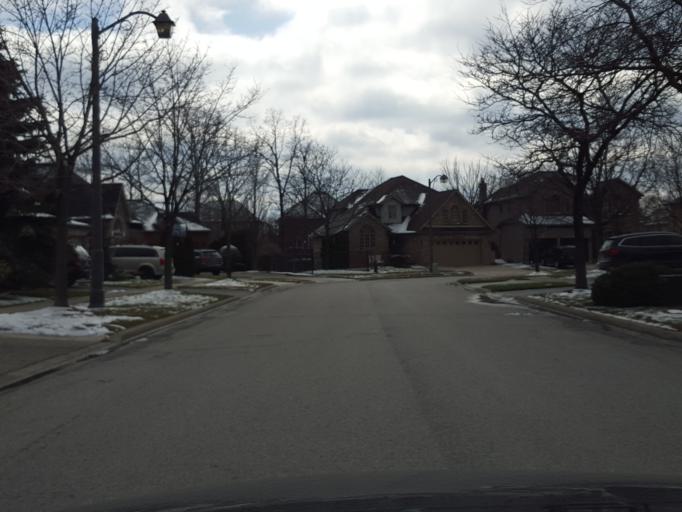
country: CA
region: Ontario
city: Burlington
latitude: 43.3869
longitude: -79.8003
